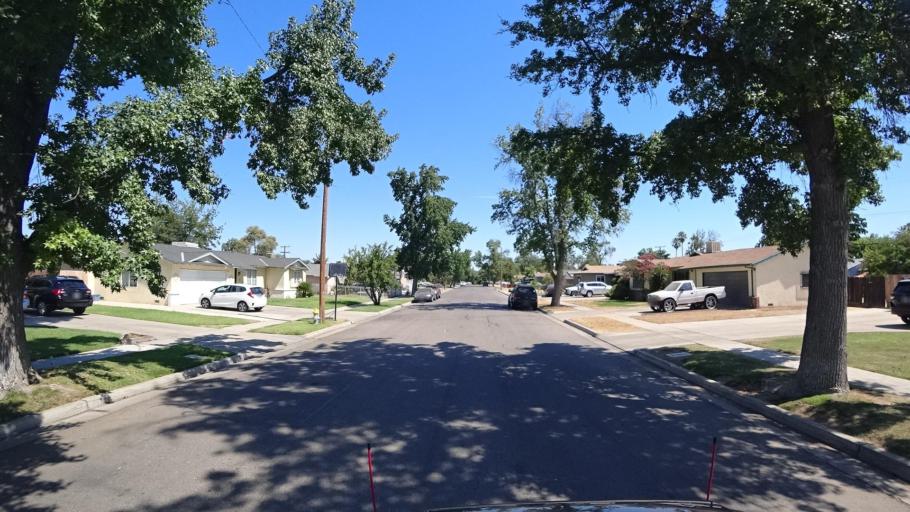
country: US
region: California
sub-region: Fresno County
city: Fresno
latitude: 36.7234
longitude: -119.7426
